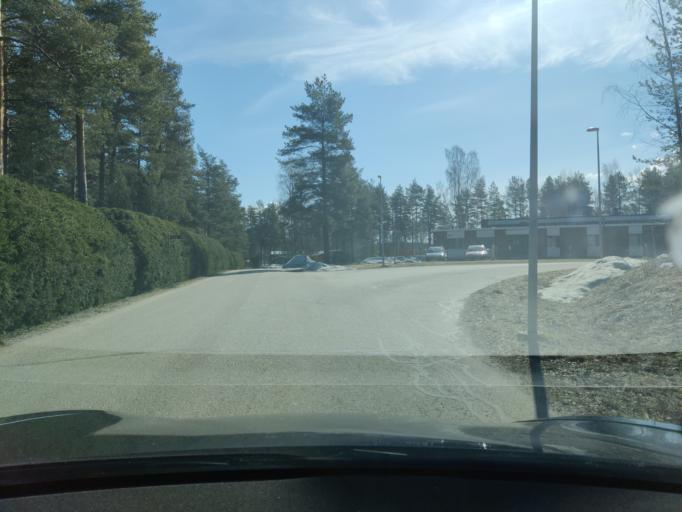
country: FI
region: Northern Savo
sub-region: Kuopio
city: Vehmersalmi
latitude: 62.7601
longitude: 28.0364
